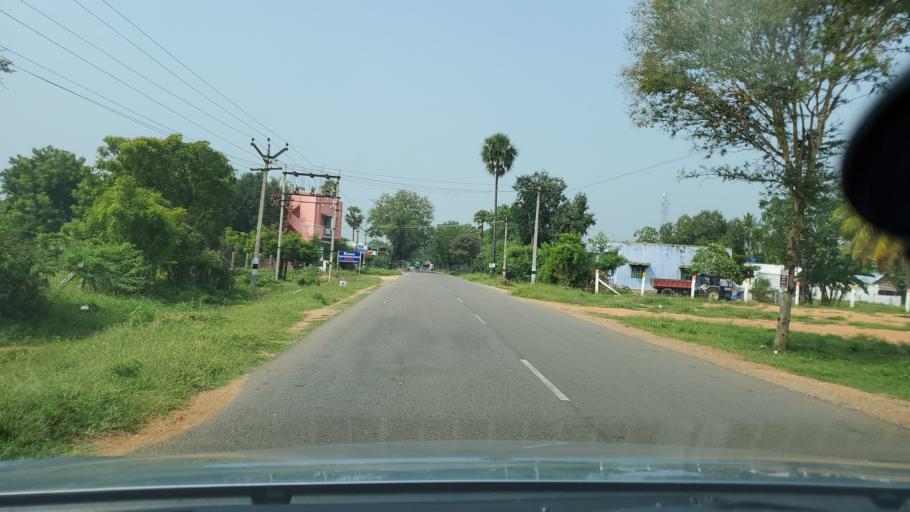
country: IN
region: Tamil Nadu
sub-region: Erode
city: Chennimalai
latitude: 11.1876
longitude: 77.6125
